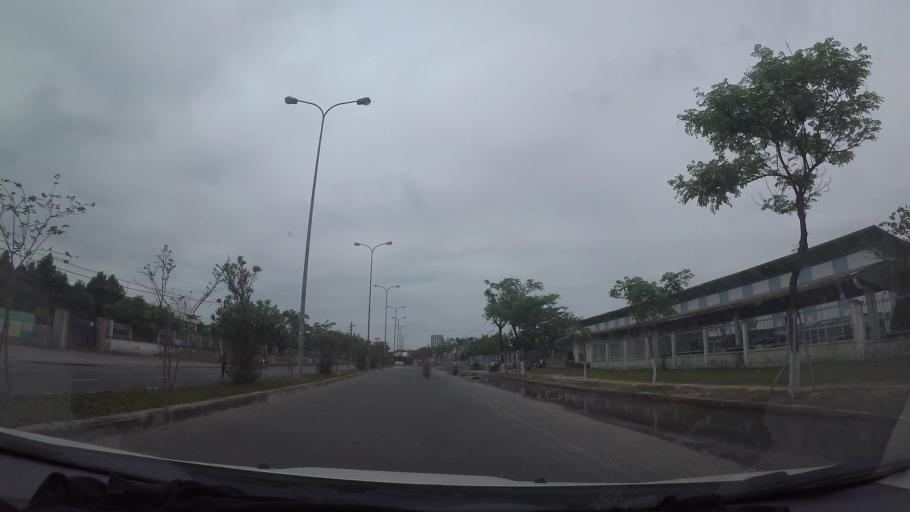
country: VN
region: Da Nang
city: Lien Chieu
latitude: 16.0762
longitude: 108.1390
